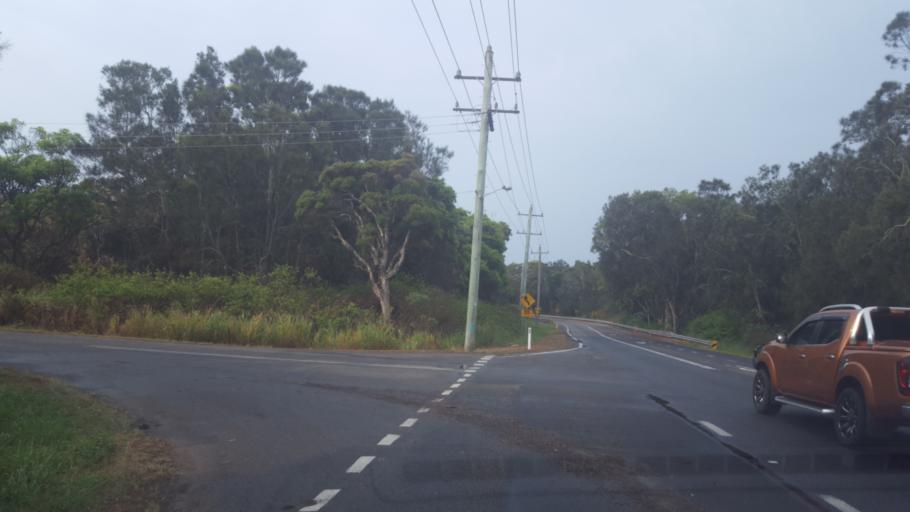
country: AU
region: New South Wales
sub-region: Port Stephens Shire
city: Anna Bay
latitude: -32.7709
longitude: 152.1149
